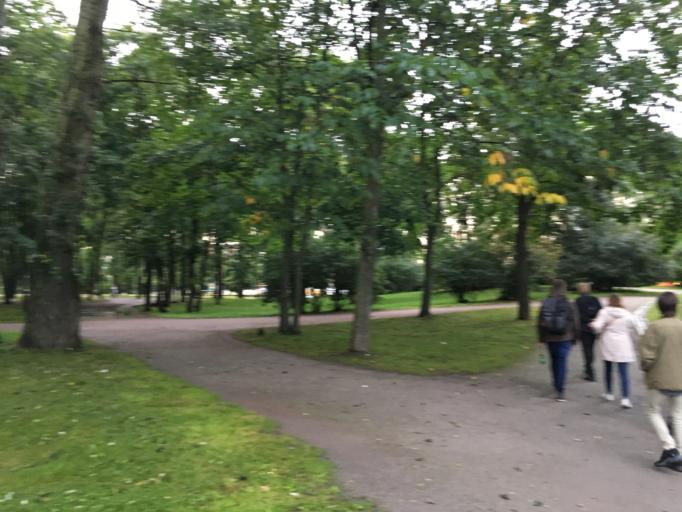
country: RU
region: Leningrad
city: Vyborg
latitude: 60.7094
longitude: 28.7469
